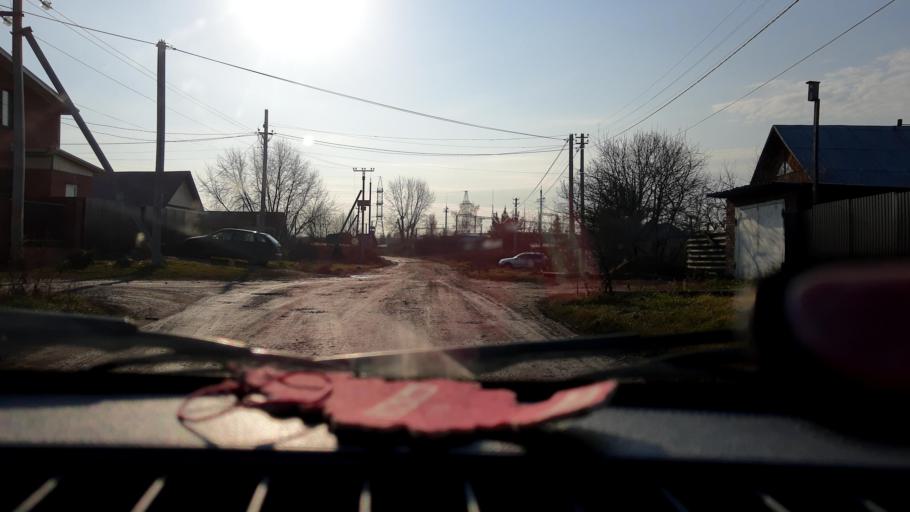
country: RU
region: Bashkortostan
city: Ufa
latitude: 54.6753
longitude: 56.0858
